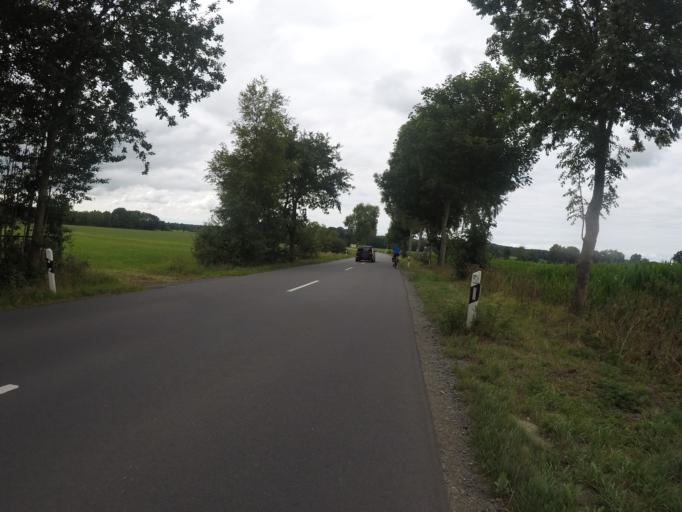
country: DE
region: Lower Saxony
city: Wingst
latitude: 53.7017
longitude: 9.0786
